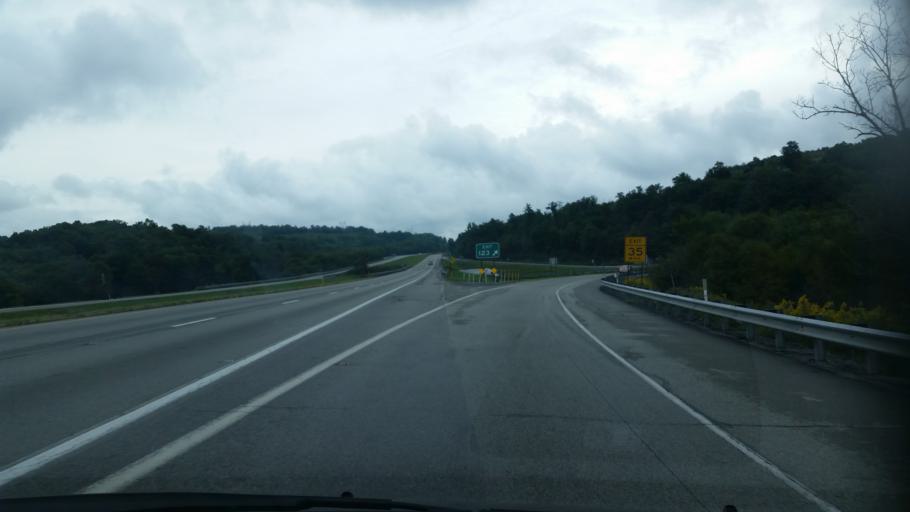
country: US
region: Pennsylvania
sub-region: Clearfield County
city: Shiloh
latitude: 41.0220
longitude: -78.3478
